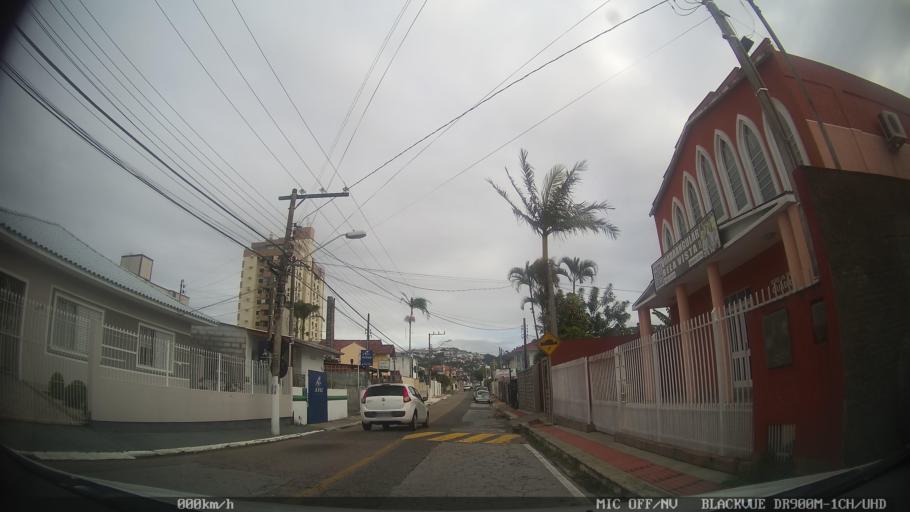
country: BR
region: Santa Catarina
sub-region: Sao Jose
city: Campinas
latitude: -27.5759
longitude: -48.6177
